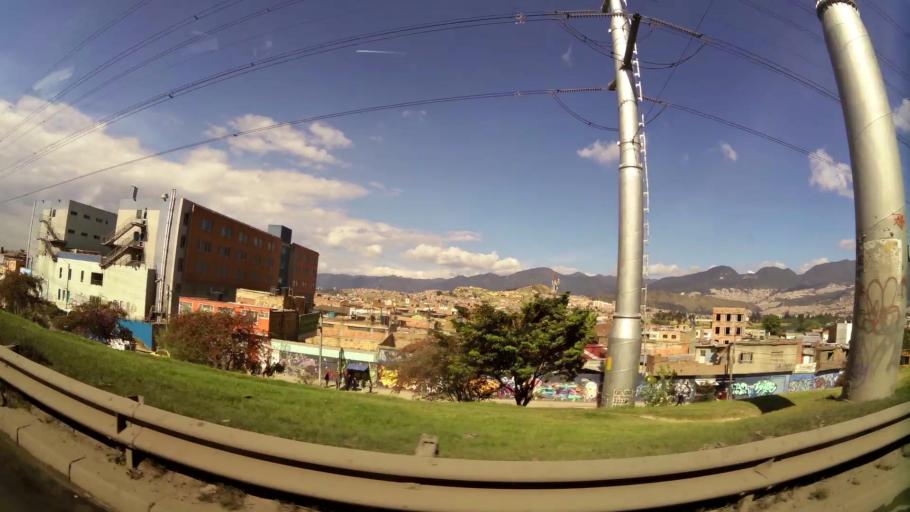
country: CO
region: Bogota D.C.
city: Bogota
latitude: 4.5586
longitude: -74.1391
